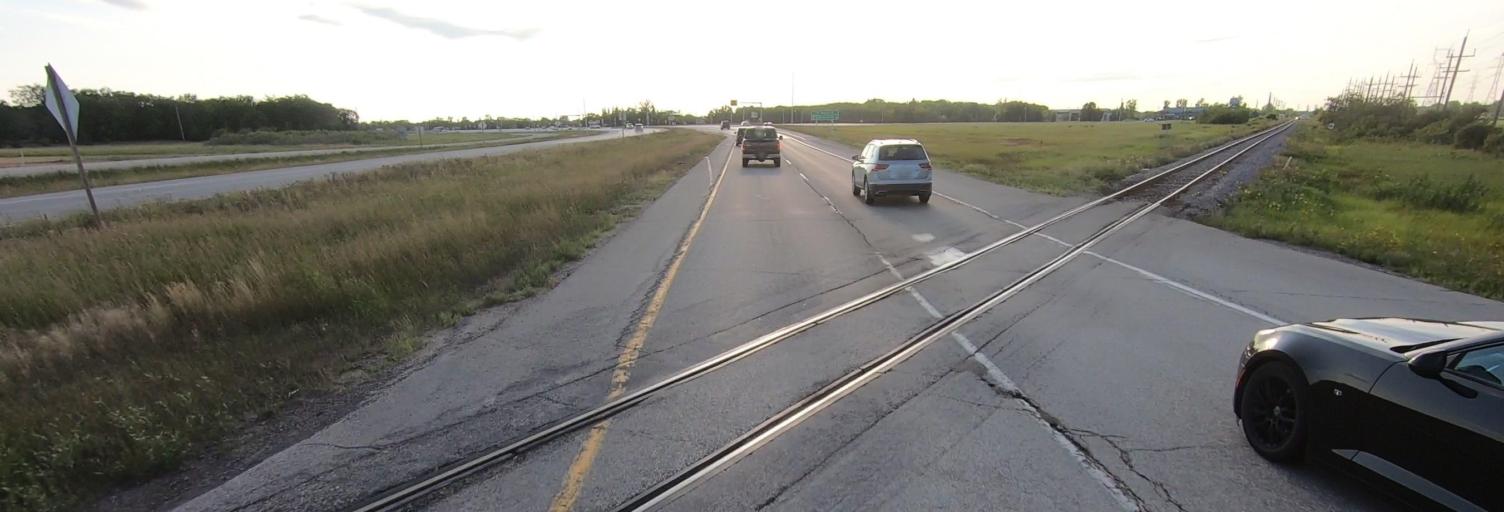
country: CA
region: Manitoba
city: Winnipeg
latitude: 49.9671
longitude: -97.0074
